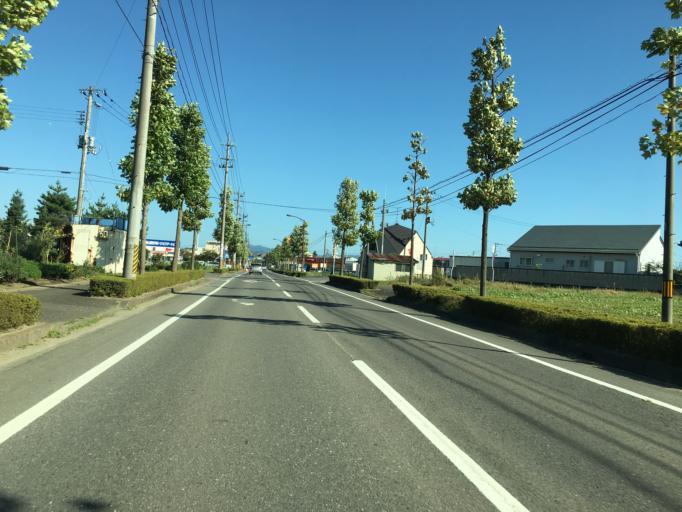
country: JP
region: Fukushima
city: Koriyama
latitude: 37.4005
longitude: 140.3215
